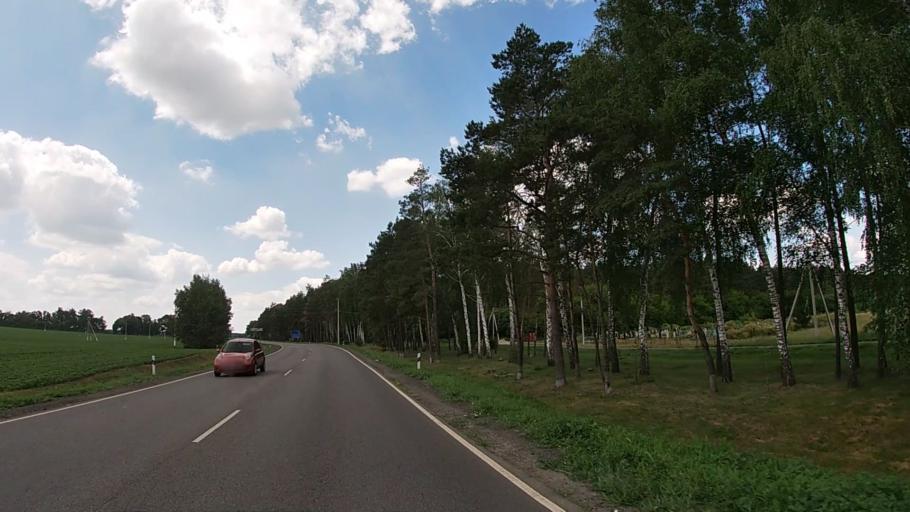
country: RU
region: Belgorod
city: Golovchino
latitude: 50.5079
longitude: 35.7473
